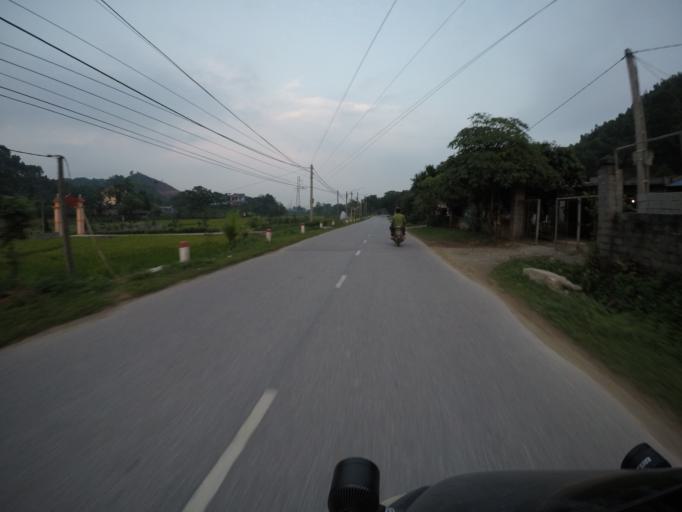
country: VN
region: Thai Nguyen
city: Chua Hang
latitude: 21.5887
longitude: 105.7308
